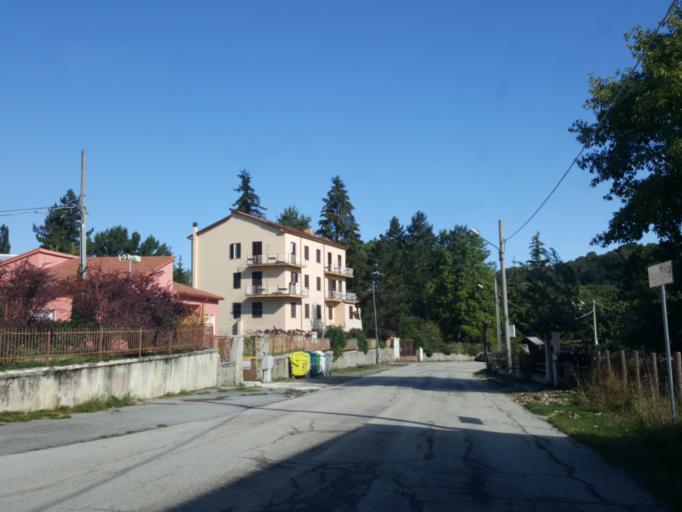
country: IT
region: Abruzzo
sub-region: Provincia dell' Aquila
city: Campotosto
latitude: 42.5614
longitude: 13.3266
